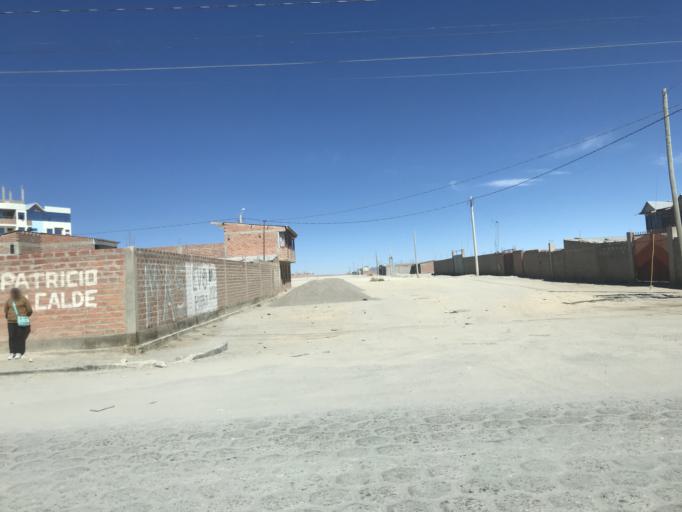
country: BO
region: Potosi
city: Uyuni
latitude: -20.4542
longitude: -66.8308
